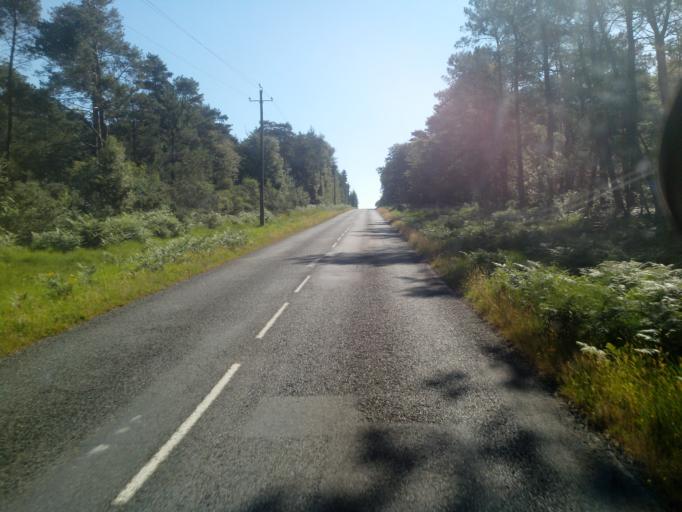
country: FR
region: Brittany
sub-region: Departement d'Ille-et-Vilaine
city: Paimpont
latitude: 48.0086
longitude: -2.2035
